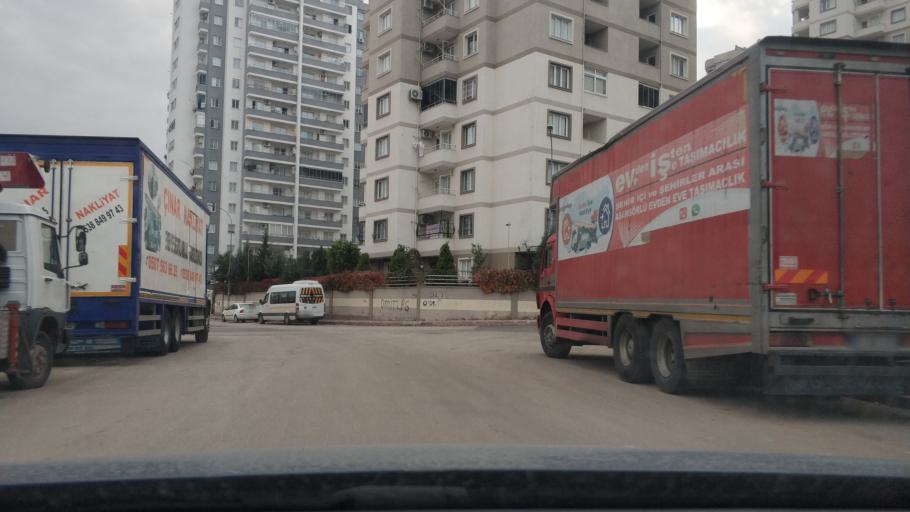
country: TR
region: Adana
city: Seyhan
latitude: 37.0161
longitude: 35.2902
